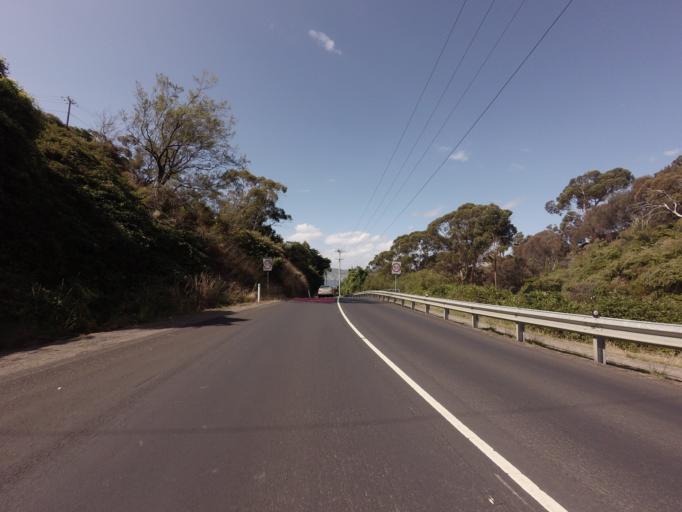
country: AU
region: Tasmania
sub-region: Hobart
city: Dynnyrne
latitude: -42.9050
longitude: 147.3172
